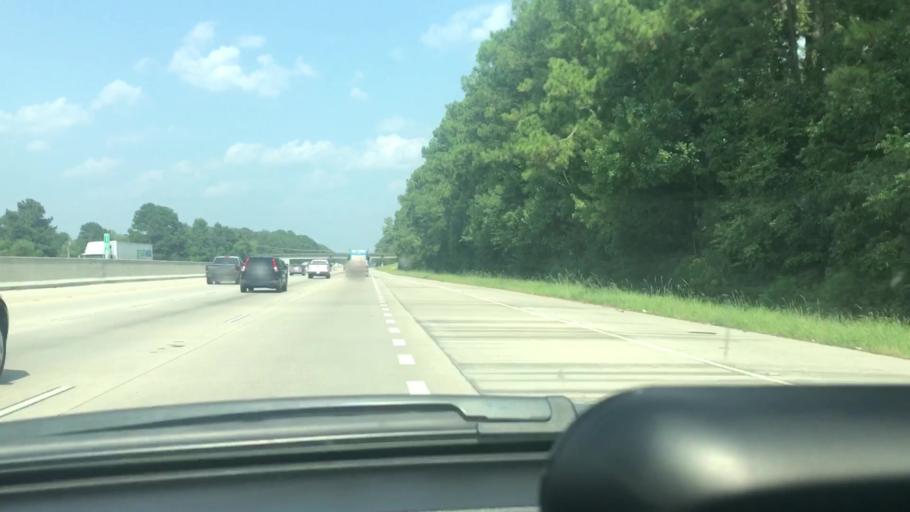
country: US
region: Louisiana
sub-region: Livingston Parish
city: Denham Springs
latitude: 30.4563
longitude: -90.9507
